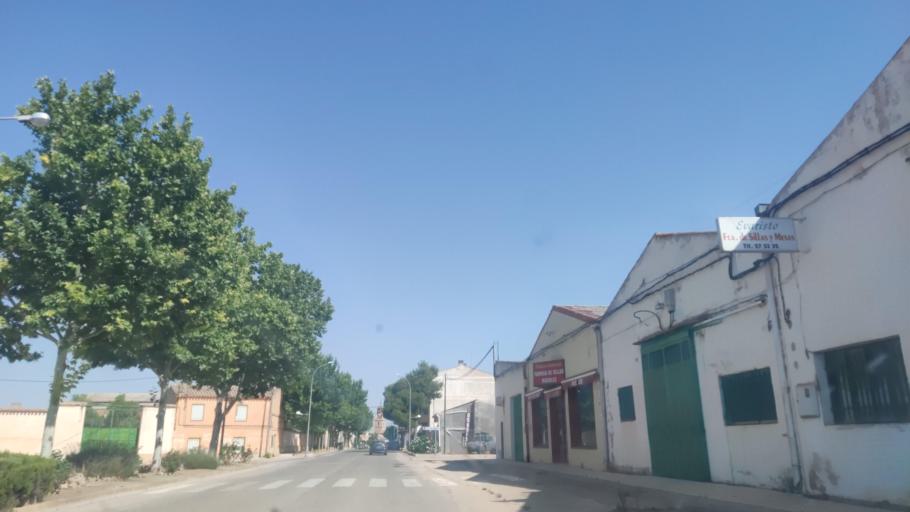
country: ES
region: Castille-La Mancha
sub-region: Provincia de Albacete
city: La Gineta
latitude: 39.1098
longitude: -1.9927
